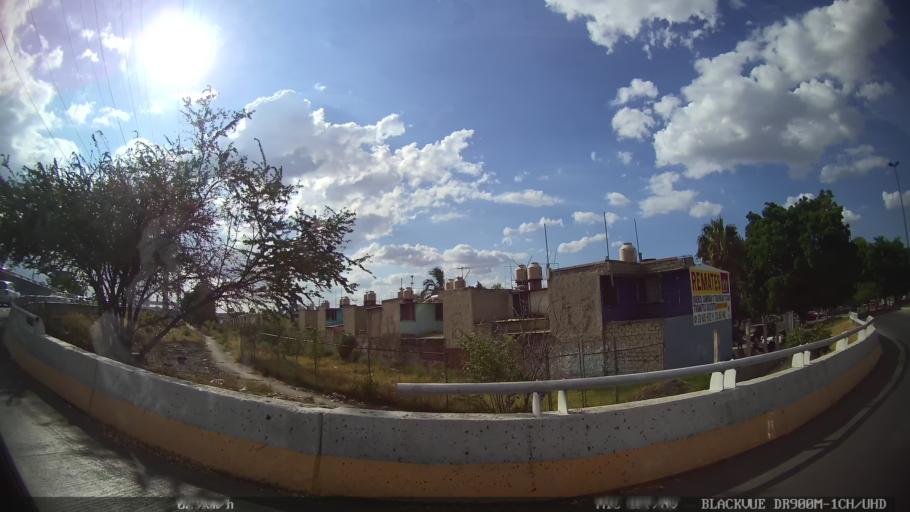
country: MX
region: Jalisco
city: Tlaquepaque
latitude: 20.6274
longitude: -103.2870
